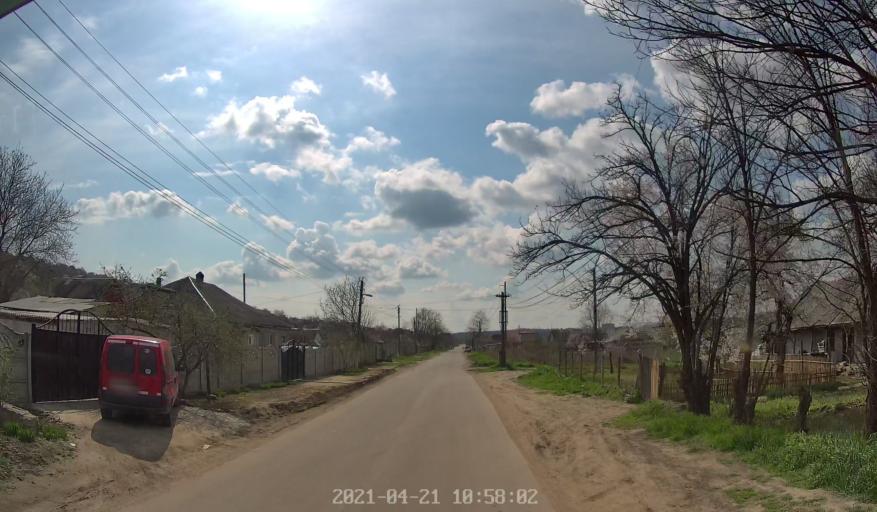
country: MD
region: Chisinau
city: Singera
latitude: 46.9564
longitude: 28.9410
